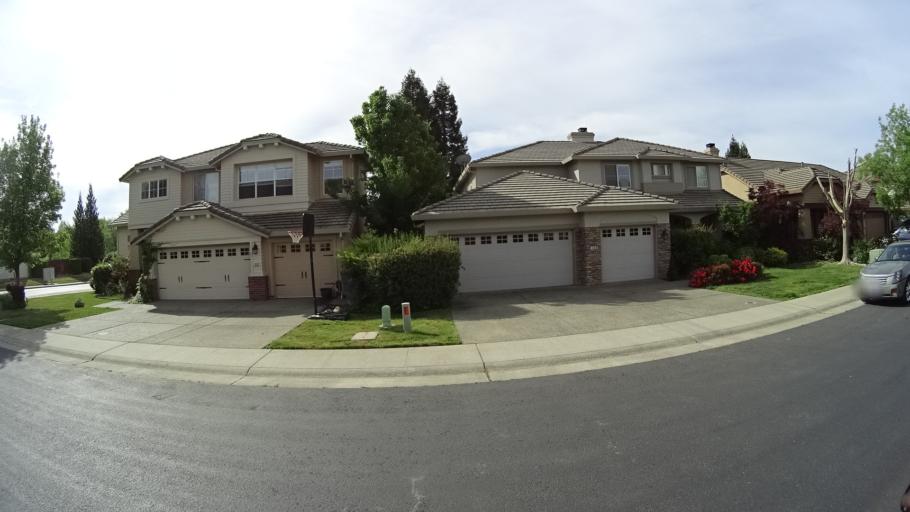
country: US
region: California
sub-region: Placer County
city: Rocklin
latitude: 38.8237
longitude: -121.2729
